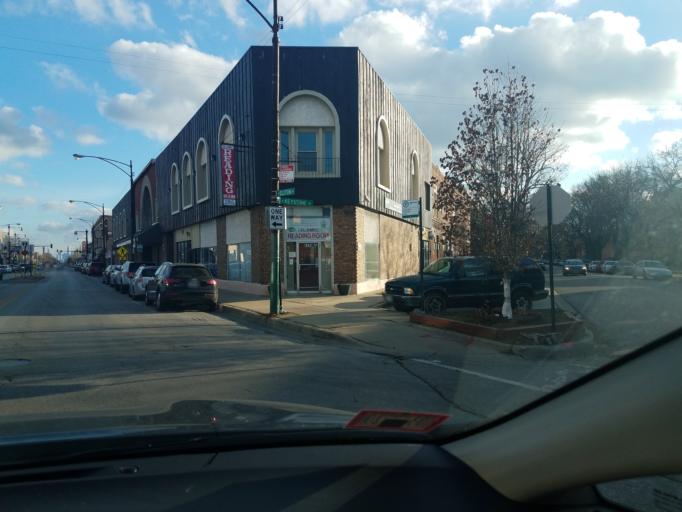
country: US
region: Illinois
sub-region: Cook County
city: Lincolnwood
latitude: 41.9607
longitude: -87.7293
